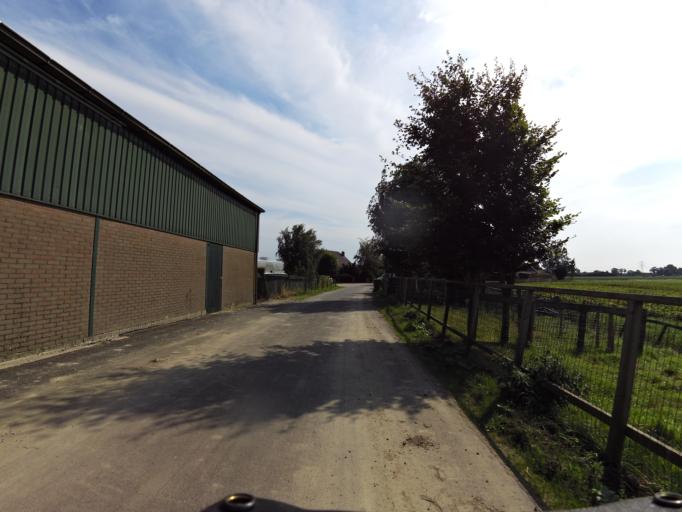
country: NL
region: South Holland
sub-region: Gemeente Binnenmaas
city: Heinenoord
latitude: 51.8235
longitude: 4.5128
